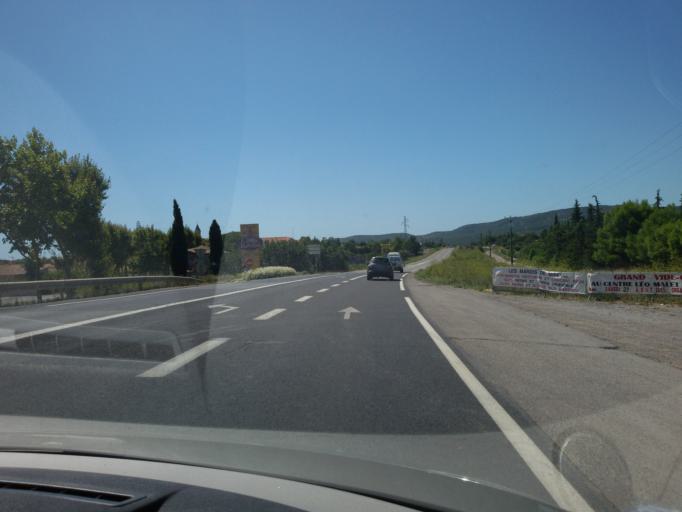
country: FR
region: Languedoc-Roussillon
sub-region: Departement de l'Herault
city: Mireval
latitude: 43.5135
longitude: 3.8051
